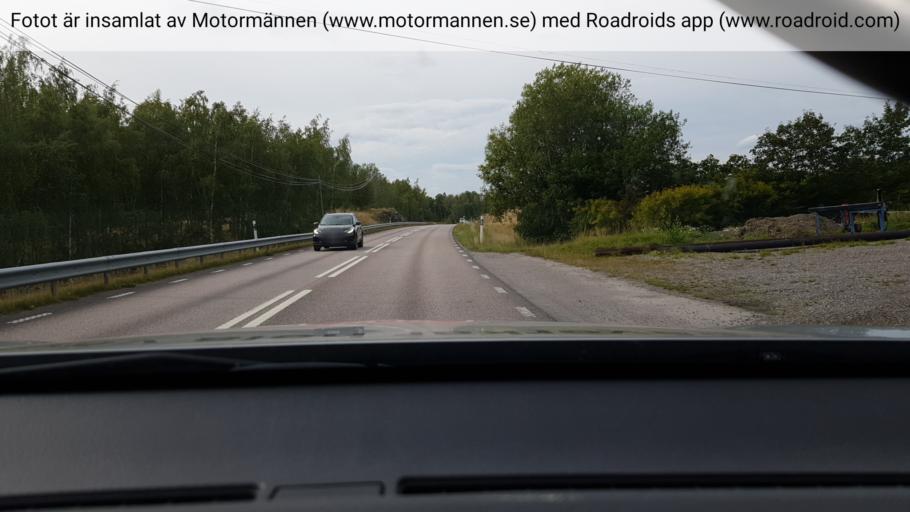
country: SE
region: Soedermanland
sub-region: Gnesta Kommun
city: Gnesta
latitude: 59.0540
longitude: 17.2456
